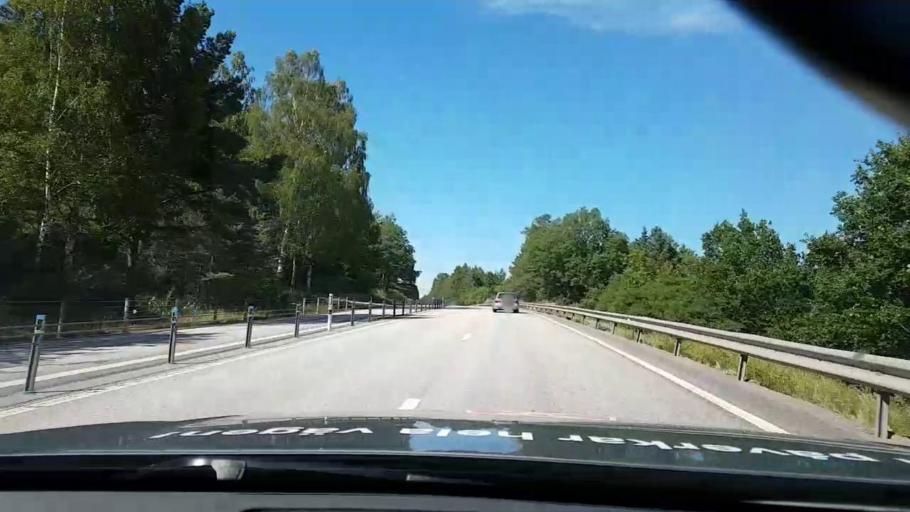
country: SE
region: Kalmar
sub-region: Vasterviks Kommun
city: Gamleby
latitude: 57.8935
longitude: 16.3868
